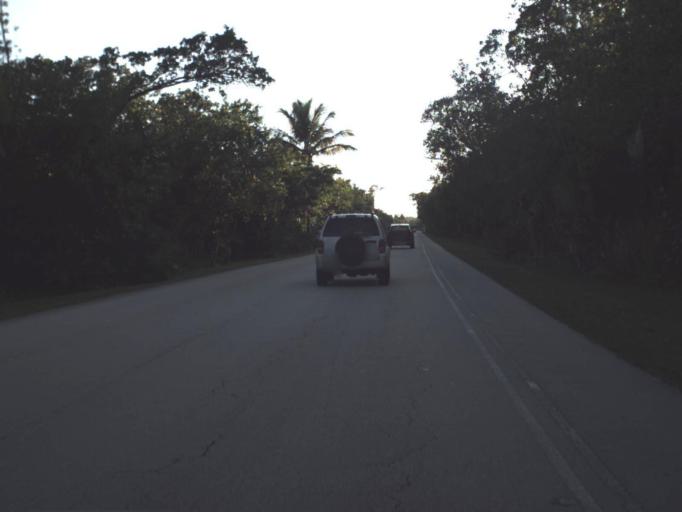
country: US
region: Florida
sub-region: Miami-Dade County
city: Key Biscayne
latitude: 25.7188
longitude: -80.1516
